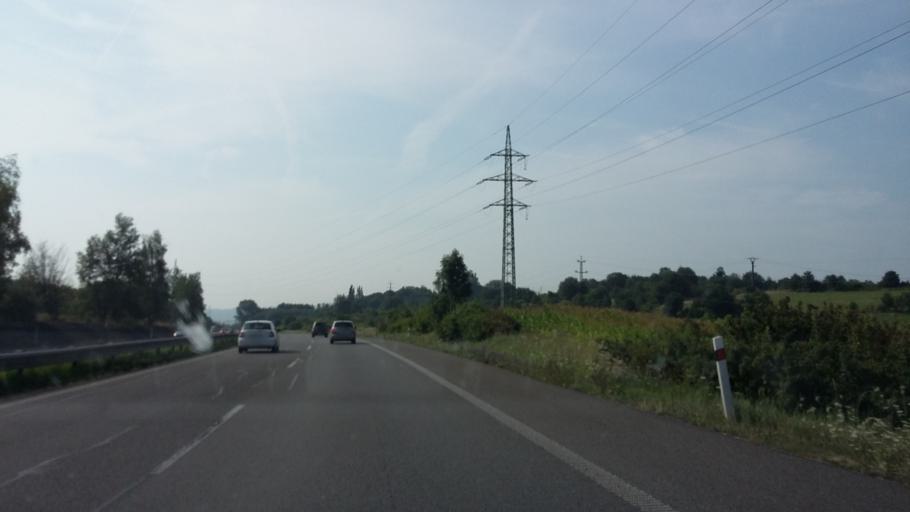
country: CZ
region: Central Bohemia
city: Kosmonosy
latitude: 50.4524
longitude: 14.9358
